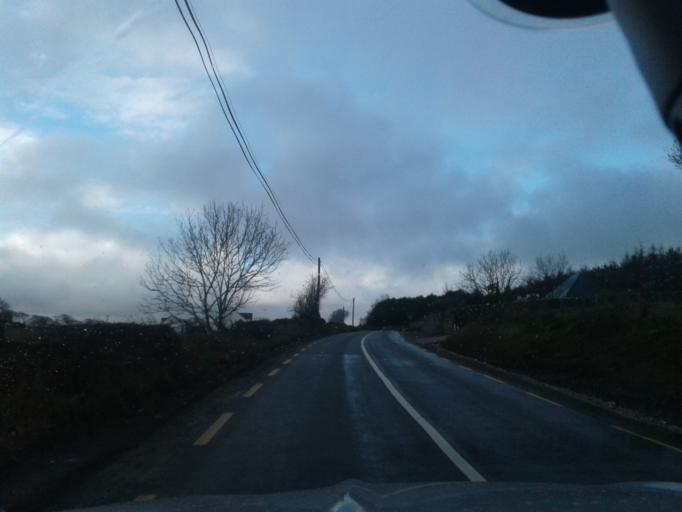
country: IE
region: Ulster
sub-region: County Donegal
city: Ramelton
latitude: 55.0093
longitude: -7.6567
